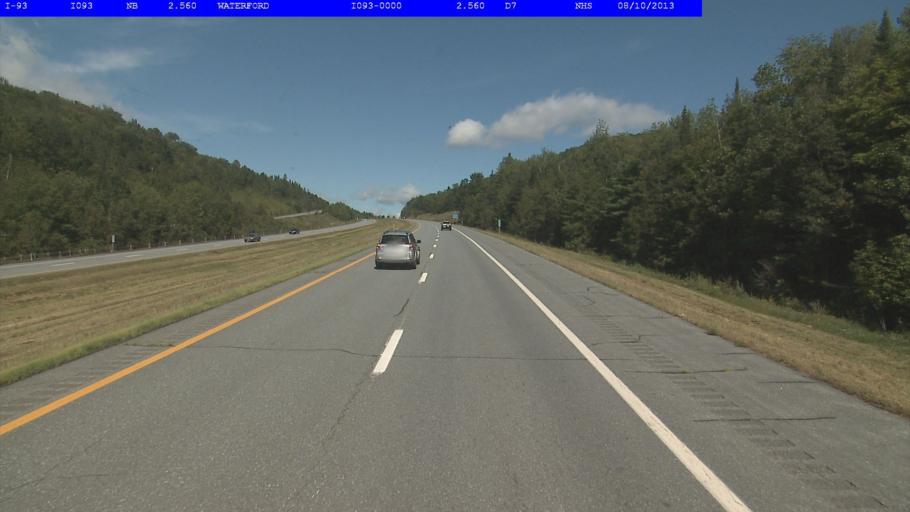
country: US
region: Vermont
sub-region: Caledonia County
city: Saint Johnsbury
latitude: 44.3763
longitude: -71.9120
